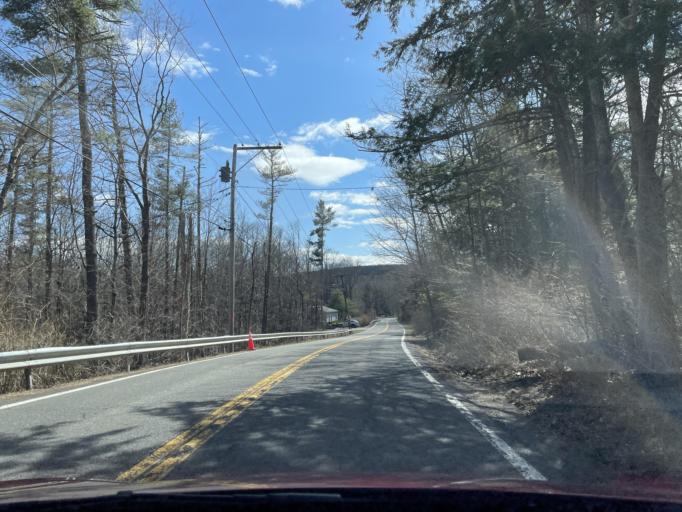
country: US
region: New York
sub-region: Ulster County
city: Zena
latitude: 42.0091
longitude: -74.0665
